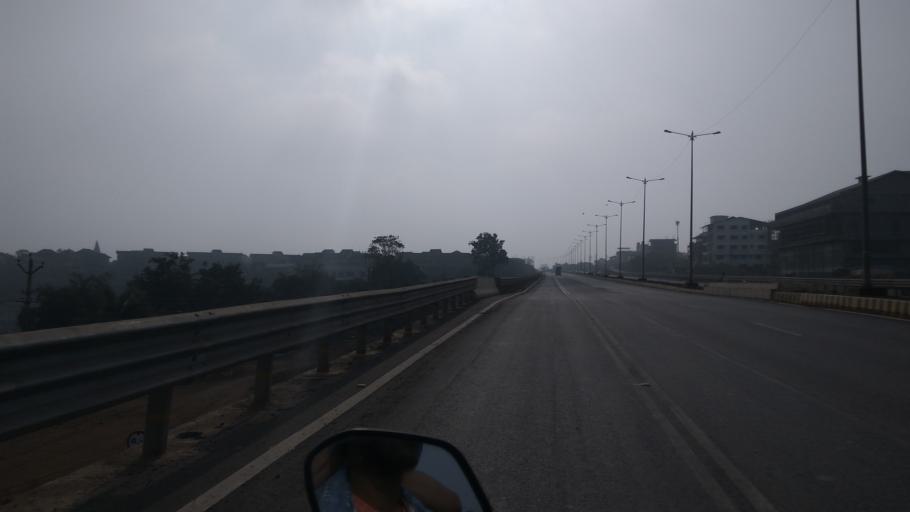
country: IN
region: Goa
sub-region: North Goa
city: Bambolim
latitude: 15.4970
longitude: 73.8785
